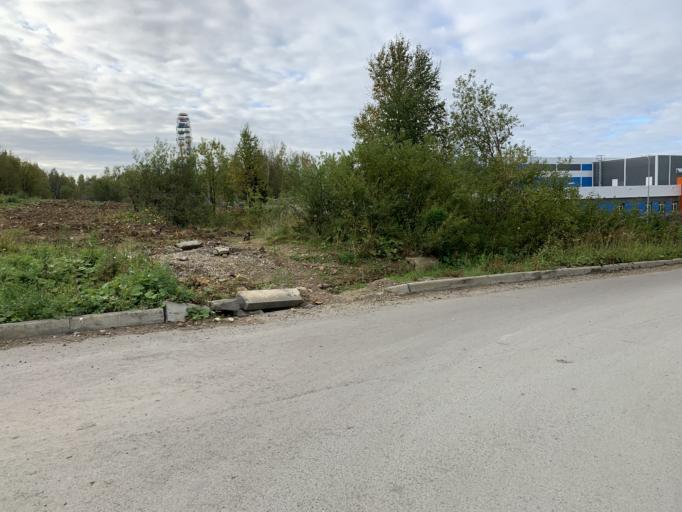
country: RU
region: Perm
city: Gubakha
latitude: 58.8348
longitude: 57.5628
